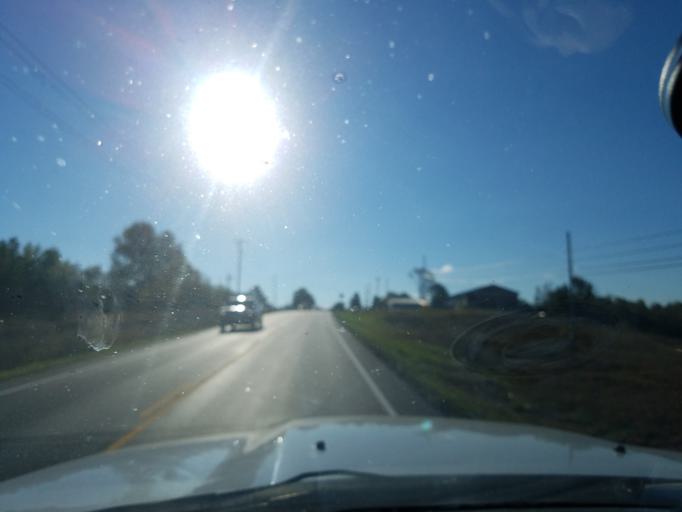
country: US
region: Kentucky
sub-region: Nelson County
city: Bardstown
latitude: 37.7834
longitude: -85.3984
